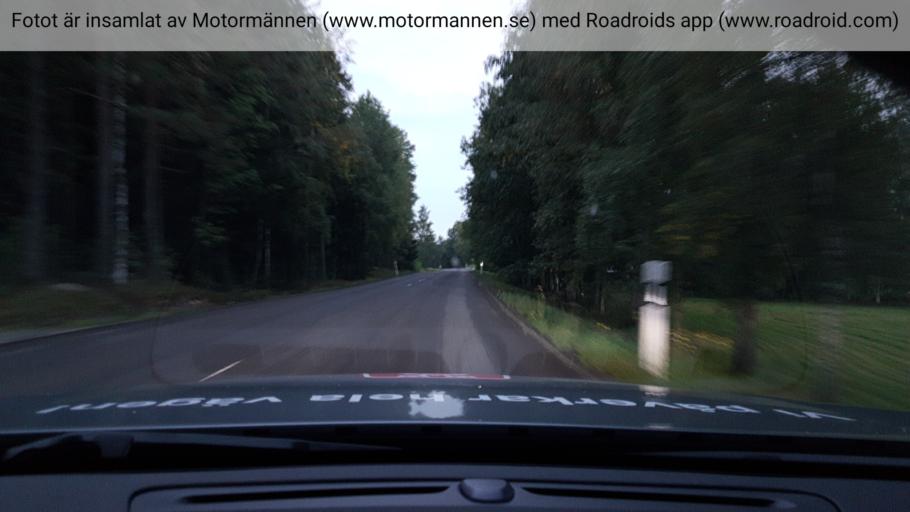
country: SE
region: OErebro
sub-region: Nora Kommun
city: As
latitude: 59.4767
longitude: 14.9160
